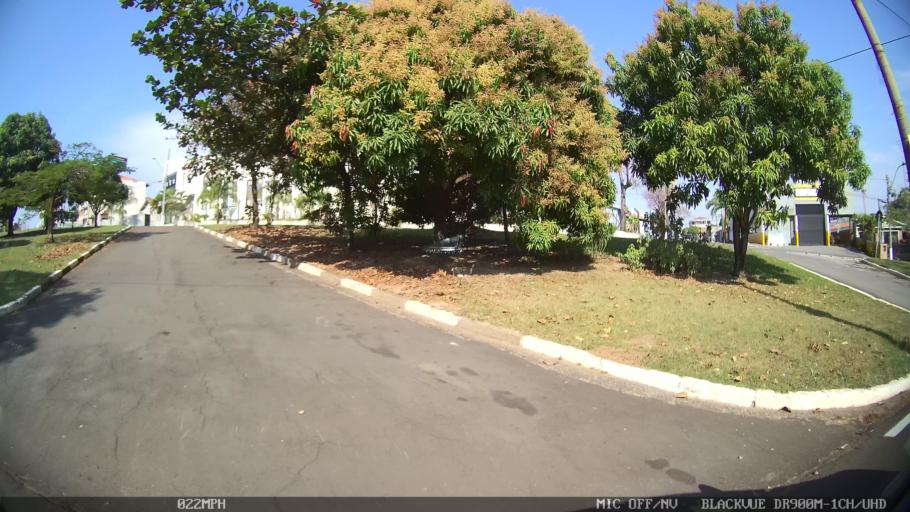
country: BR
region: Sao Paulo
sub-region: Paulinia
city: Paulinia
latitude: -22.7718
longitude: -47.1595
